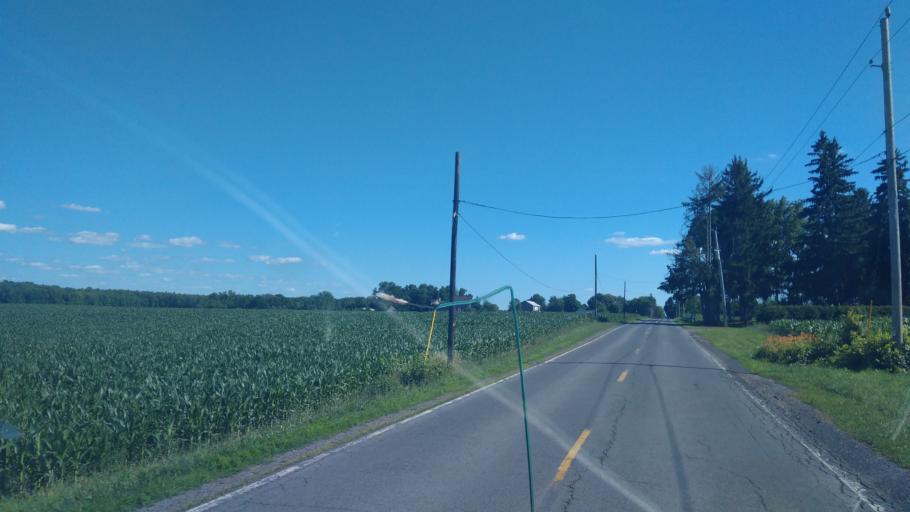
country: US
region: New York
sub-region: Seneca County
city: Seneca Falls
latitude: 42.9717
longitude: -76.7957
